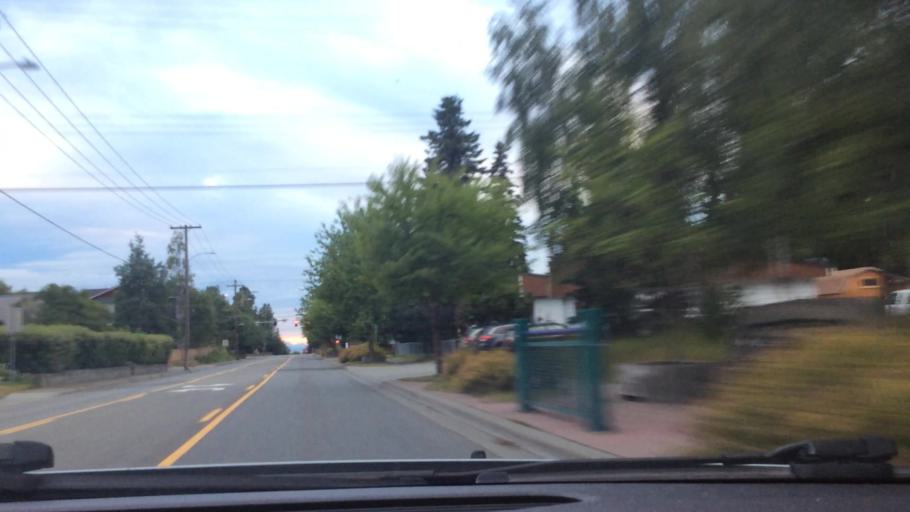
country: US
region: Alaska
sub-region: Anchorage Municipality
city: Anchorage
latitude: 61.2077
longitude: -149.8960
